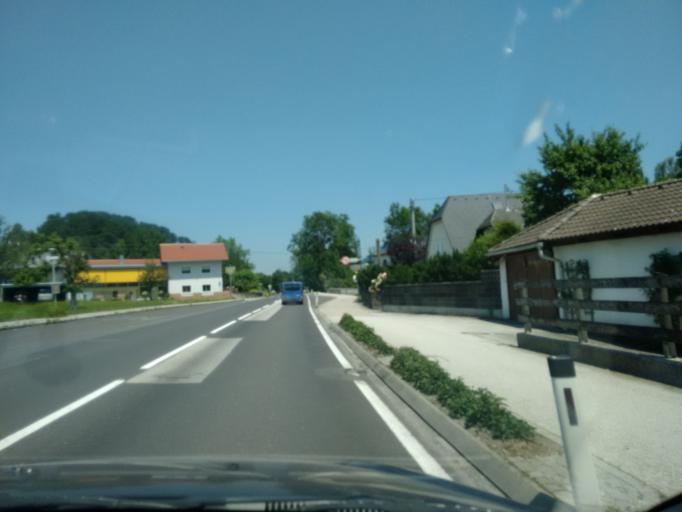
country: AT
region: Upper Austria
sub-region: Politischer Bezirk Gmunden
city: Altmunster
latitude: 47.8656
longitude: 13.7766
